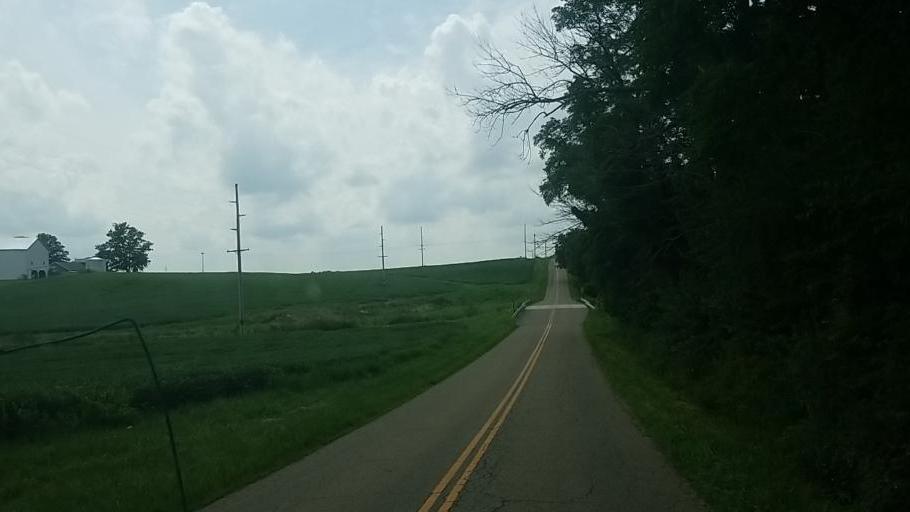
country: US
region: Ohio
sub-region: Knox County
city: Gambier
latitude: 40.3172
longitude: -82.4259
